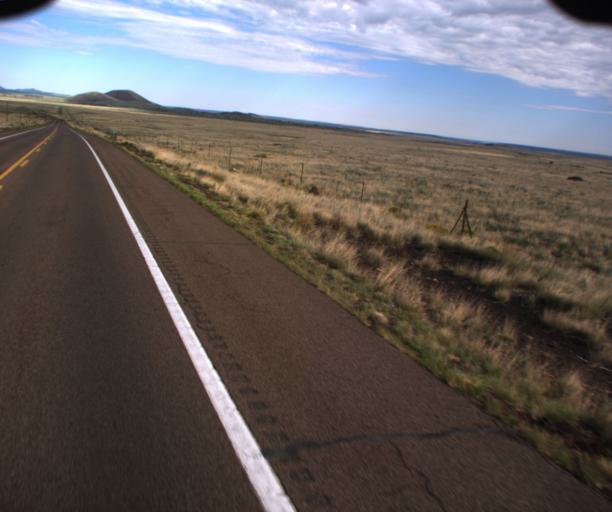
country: US
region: Arizona
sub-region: Apache County
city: Springerville
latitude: 34.1812
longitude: -109.3274
